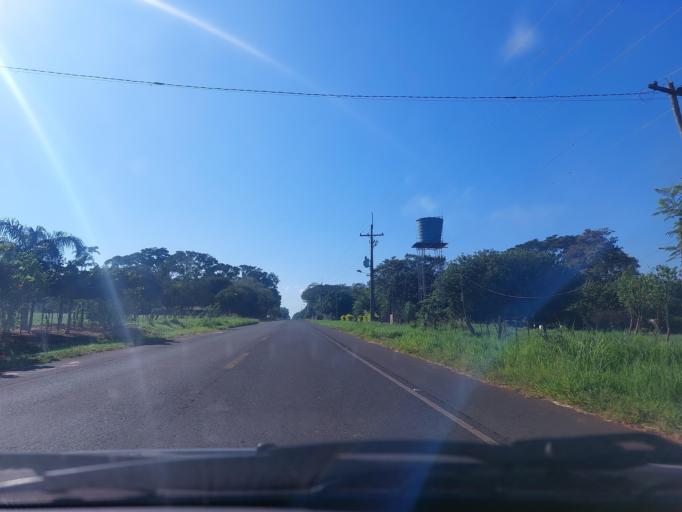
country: PY
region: San Pedro
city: Guayaybi
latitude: -24.5320
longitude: -56.5010
